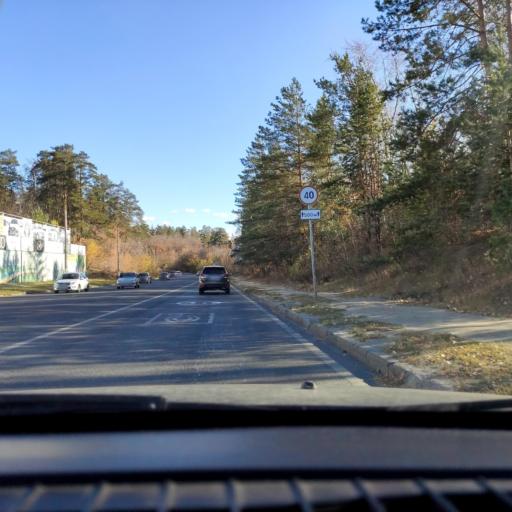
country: RU
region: Samara
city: Tol'yatti
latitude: 53.4951
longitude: 49.2897
